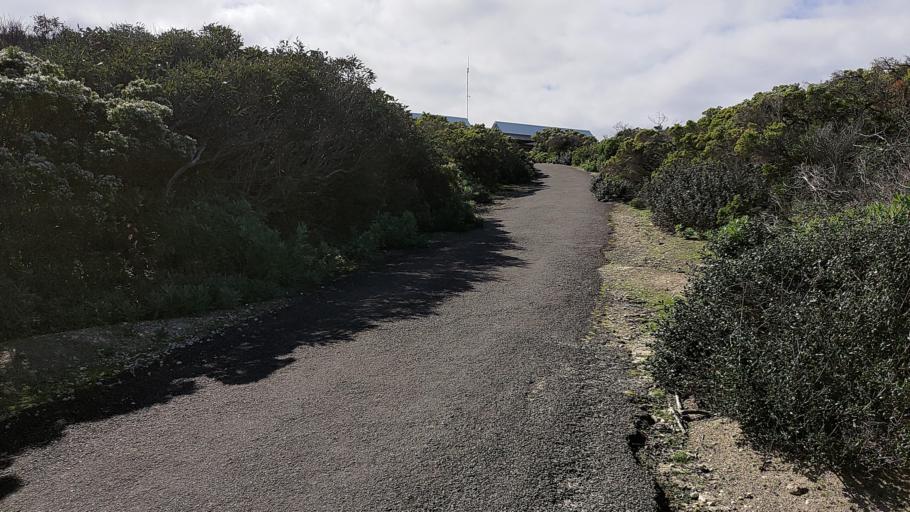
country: AU
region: South Australia
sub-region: Kangaroo Island
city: Kingscote
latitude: -35.9928
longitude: 137.3186
